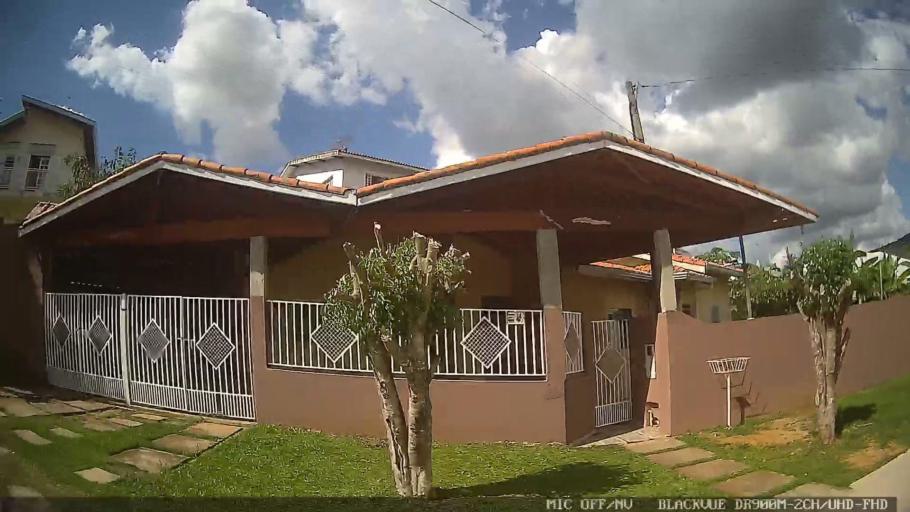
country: BR
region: Sao Paulo
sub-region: Atibaia
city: Atibaia
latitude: -23.1500
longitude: -46.5531
